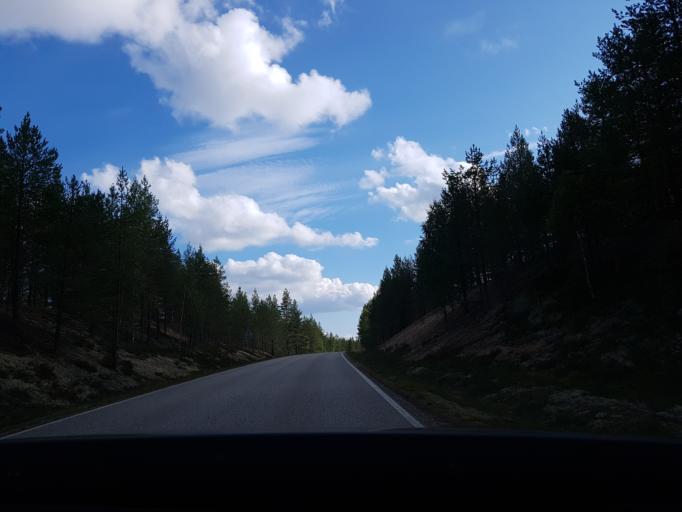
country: FI
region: Kainuu
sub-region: Kehys-Kainuu
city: Kuhmo
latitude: 64.6246
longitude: 29.6975
